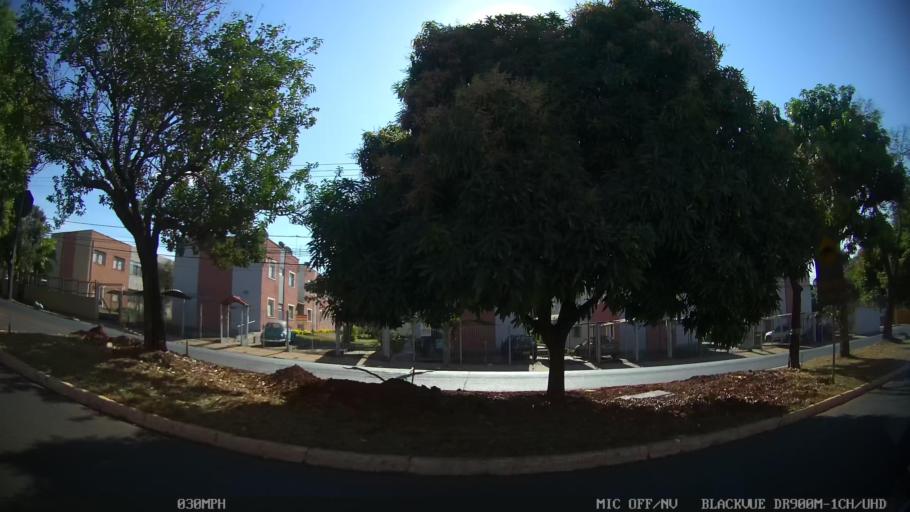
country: BR
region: Sao Paulo
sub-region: Ribeirao Preto
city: Ribeirao Preto
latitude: -21.1685
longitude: -47.7904
